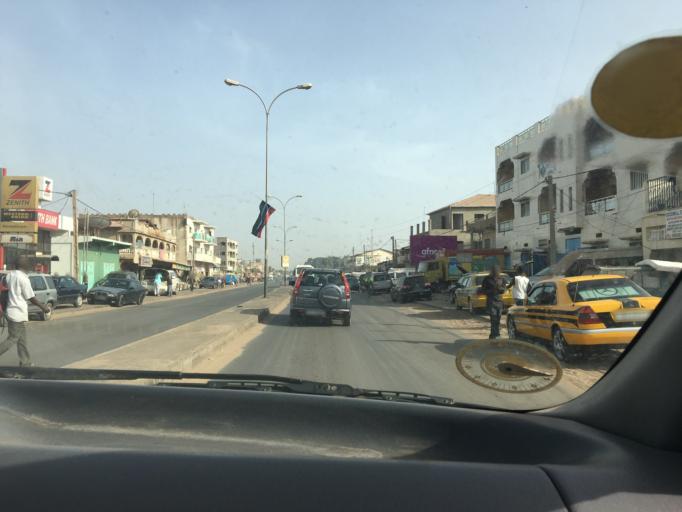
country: GM
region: Western
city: Abuko
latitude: 13.4370
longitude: -16.6766
